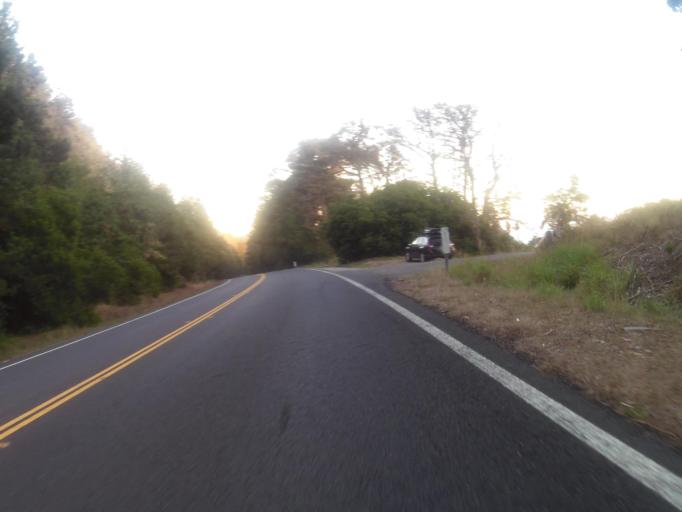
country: US
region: California
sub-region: Sonoma County
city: Sea Ranch
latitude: 38.6065
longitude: -123.3618
